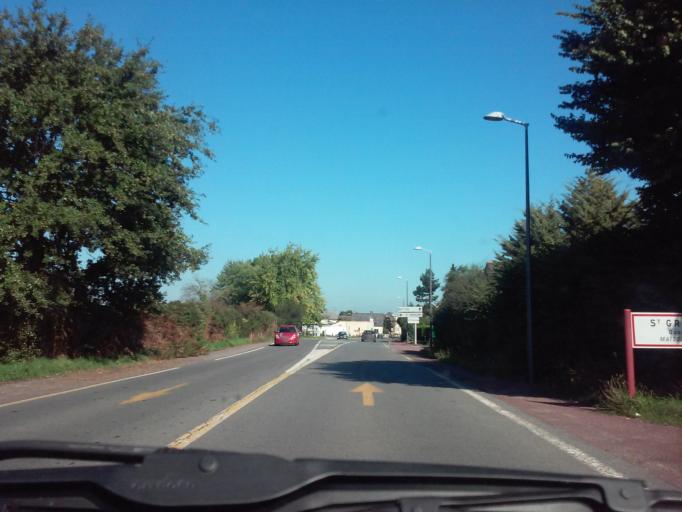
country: FR
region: Brittany
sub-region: Departement d'Ille-et-Vilaine
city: Saint-Gregoire
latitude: 48.1459
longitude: -1.6569
